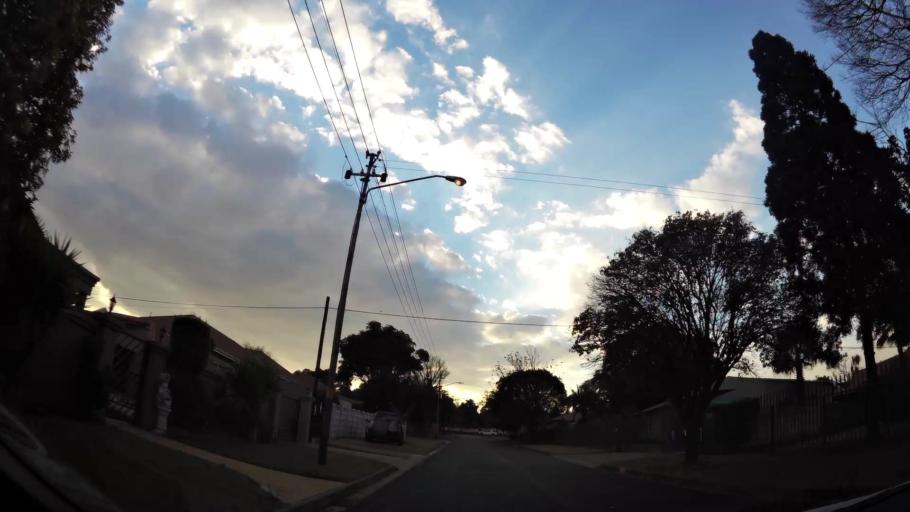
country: ZA
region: Gauteng
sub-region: Ekurhuleni Metropolitan Municipality
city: Germiston
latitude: -26.1866
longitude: 28.1564
